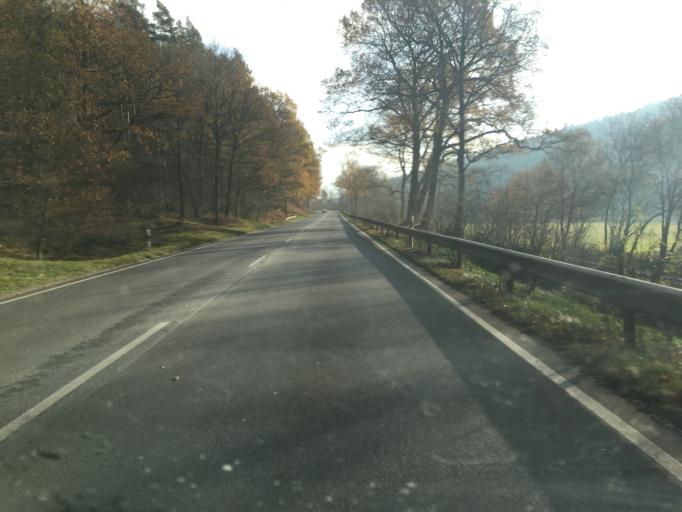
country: DE
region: North Rhine-Westphalia
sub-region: Regierungsbezirk Koln
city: Kall
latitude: 50.5648
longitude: 6.5325
